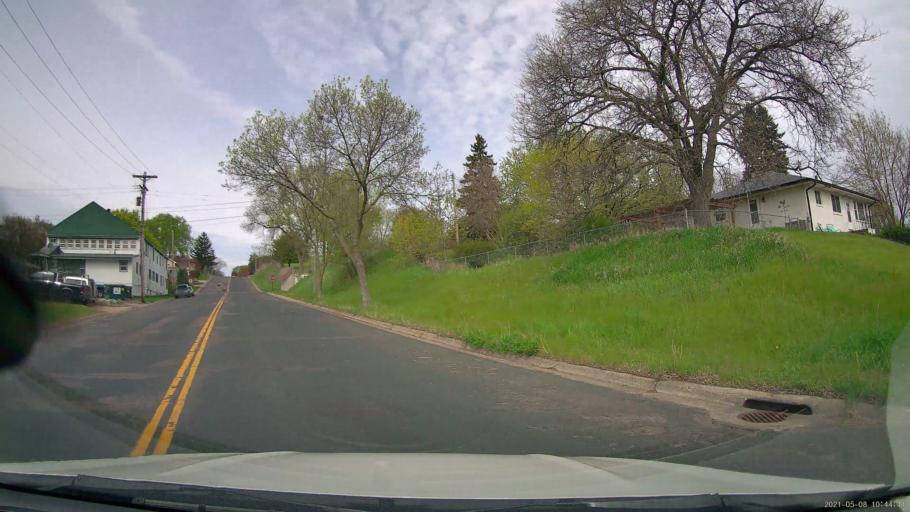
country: US
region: Minnesota
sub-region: Dakota County
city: South Saint Paul
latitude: 44.8907
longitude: -93.0513
